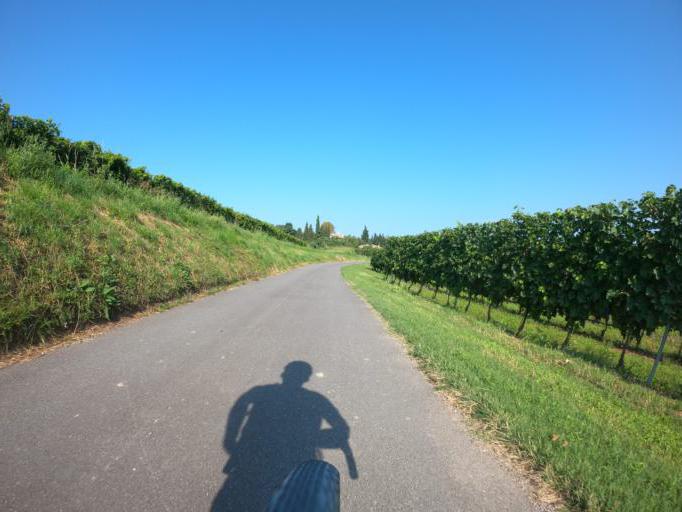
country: IT
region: Veneto
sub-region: Provincia di Verona
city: Calmasino
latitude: 45.5029
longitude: 10.7608
